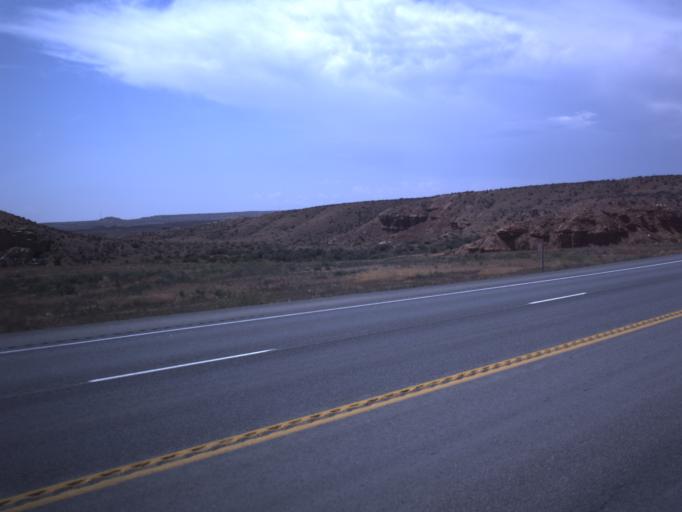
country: US
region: Utah
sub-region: Uintah County
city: Maeser
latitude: 40.3371
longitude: -109.6341
